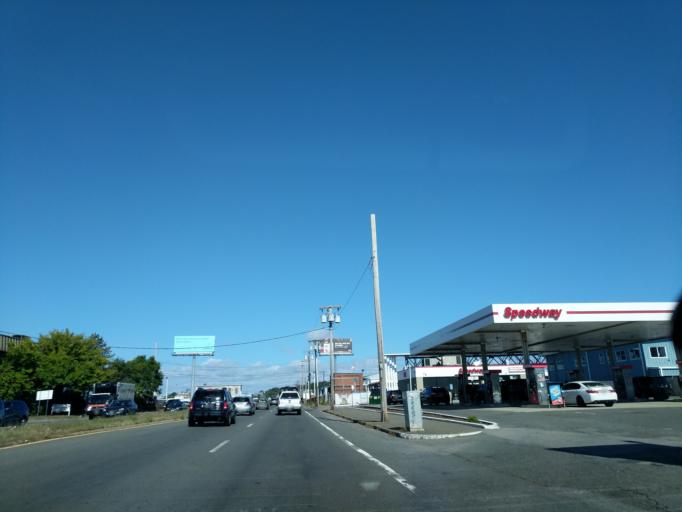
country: US
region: Massachusetts
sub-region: Suffolk County
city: Revere
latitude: 42.3958
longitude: -71.0096
